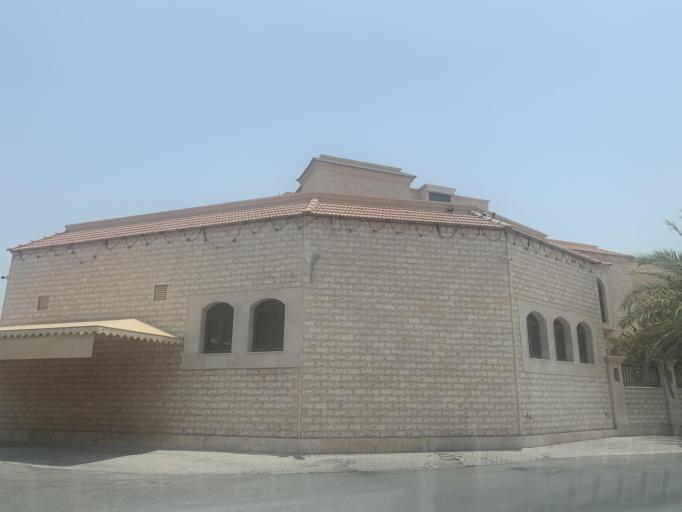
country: BH
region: Manama
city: Jidd Hafs
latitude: 26.2216
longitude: 50.4585
